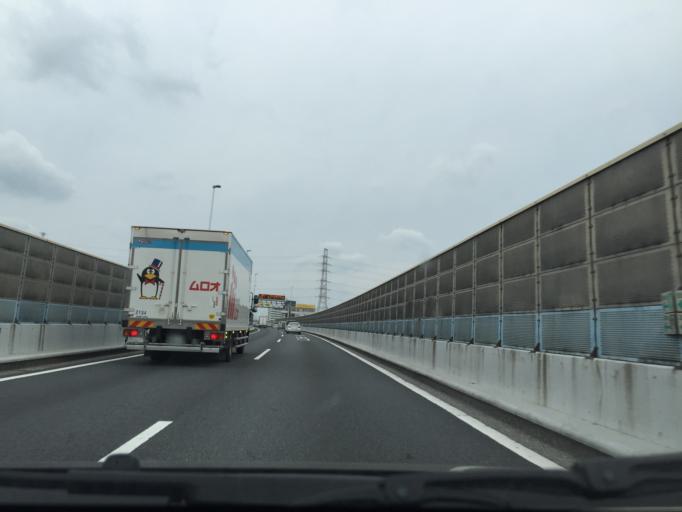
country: JP
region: Saitama
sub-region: Kawaguchi-shi
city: Hatogaya-honcho
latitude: 35.8108
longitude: 139.7590
